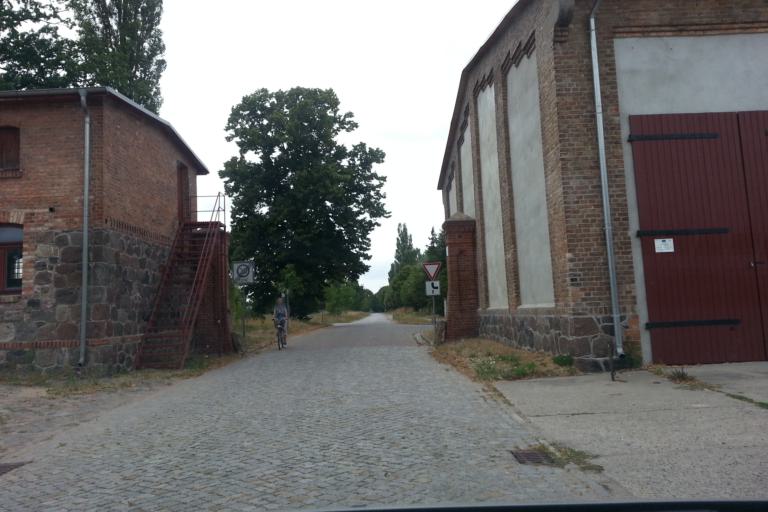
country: DE
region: Mecklenburg-Vorpommern
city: Ferdinandshof
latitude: 53.6656
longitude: 13.8847
